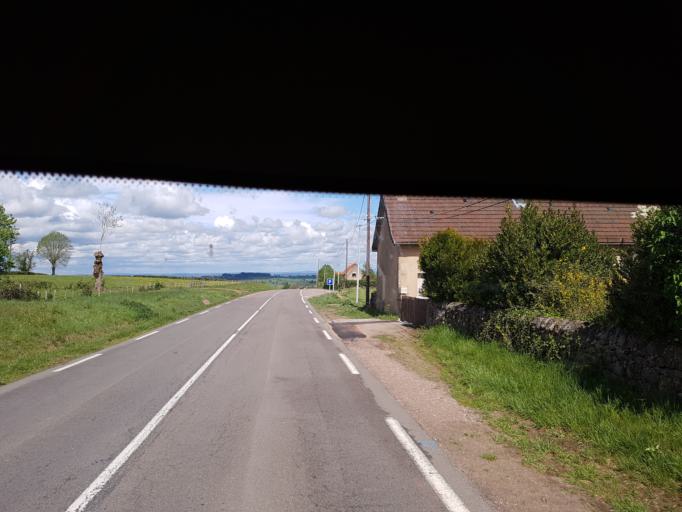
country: FR
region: Bourgogne
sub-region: Departement de Saone-et-Loire
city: La Clayette
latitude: 46.3467
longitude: 4.2692
